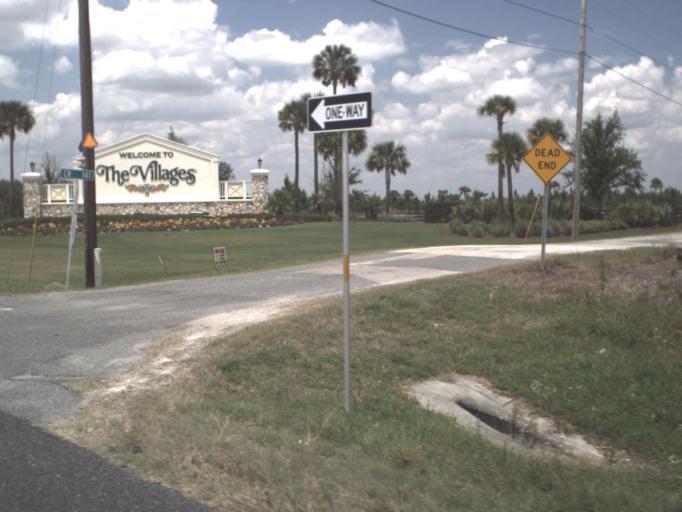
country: US
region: Florida
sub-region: Lake County
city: Fruitland Park
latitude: 28.8216
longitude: -81.9581
